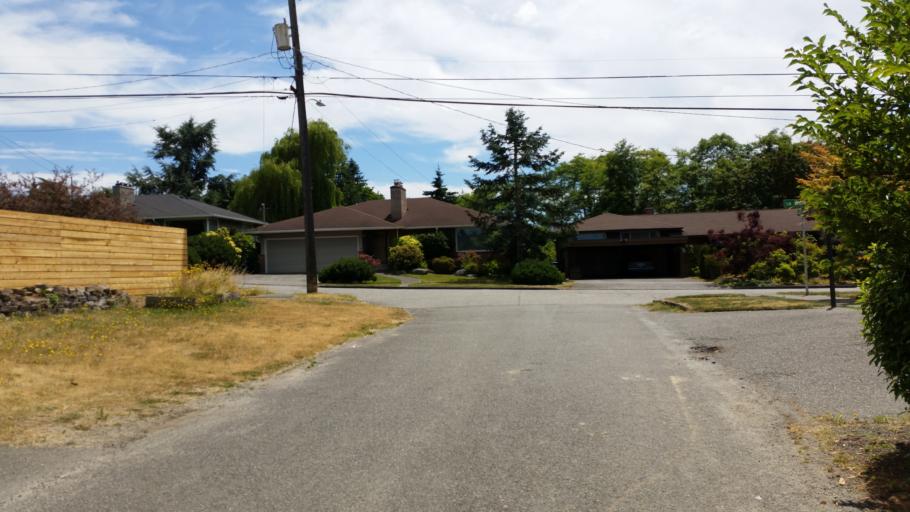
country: US
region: Washington
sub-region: King County
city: Seattle
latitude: 47.5843
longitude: -122.3930
